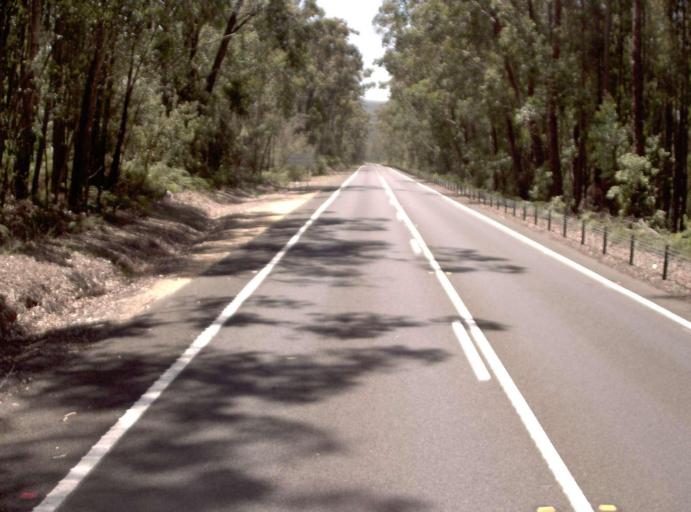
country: AU
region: Victoria
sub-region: East Gippsland
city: Lakes Entrance
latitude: -37.7450
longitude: 148.0739
